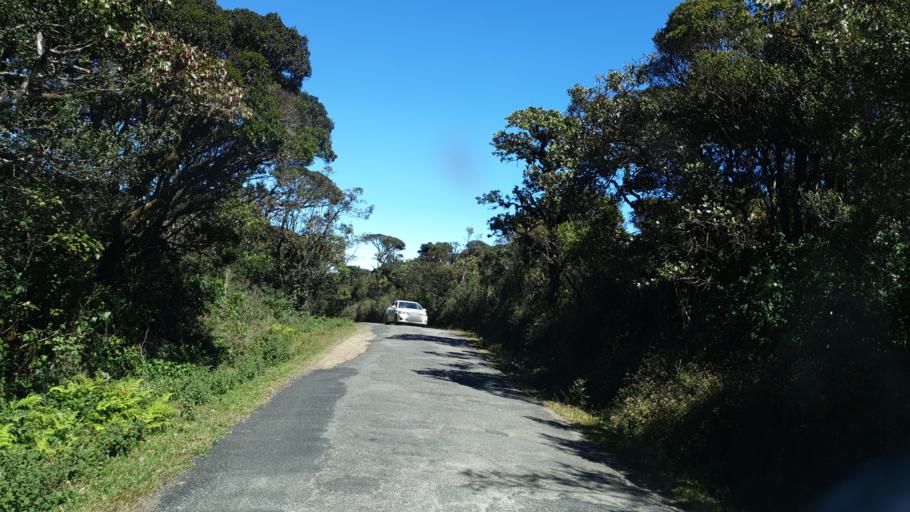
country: LK
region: Central
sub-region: Nuwara Eliya District
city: Nuwara Eliya
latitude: 6.8357
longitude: 80.8106
